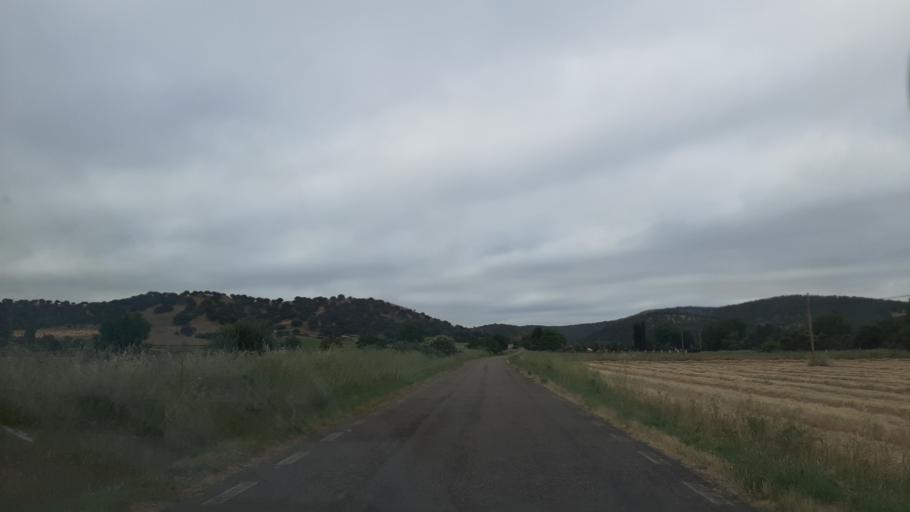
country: ES
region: Castille and Leon
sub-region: Provincia de Salamanca
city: Pastores
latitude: 40.5576
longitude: -6.4867
